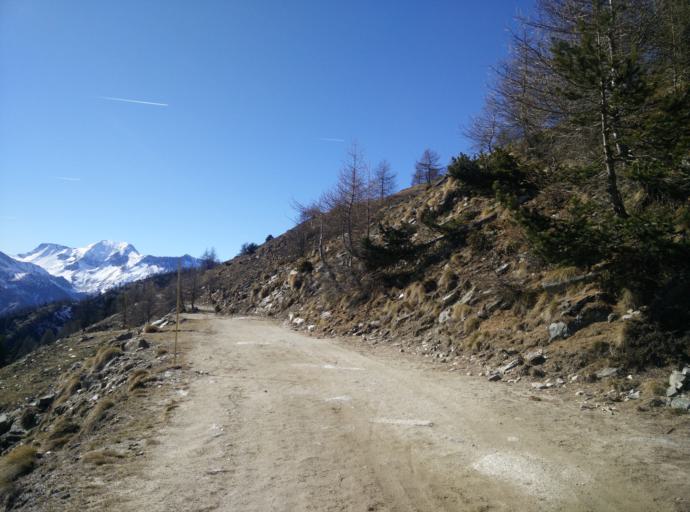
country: IT
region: Piedmont
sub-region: Provincia di Torino
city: Roure
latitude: 45.0453
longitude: 7.1165
